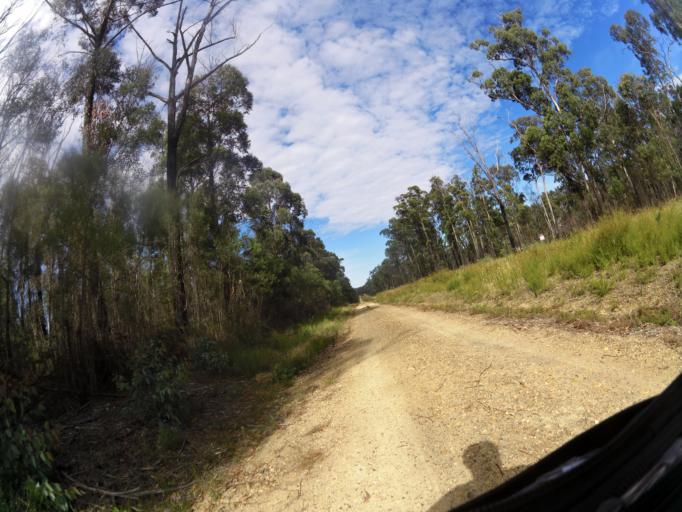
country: AU
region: Victoria
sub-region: East Gippsland
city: Lakes Entrance
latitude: -37.7465
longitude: 148.2341
